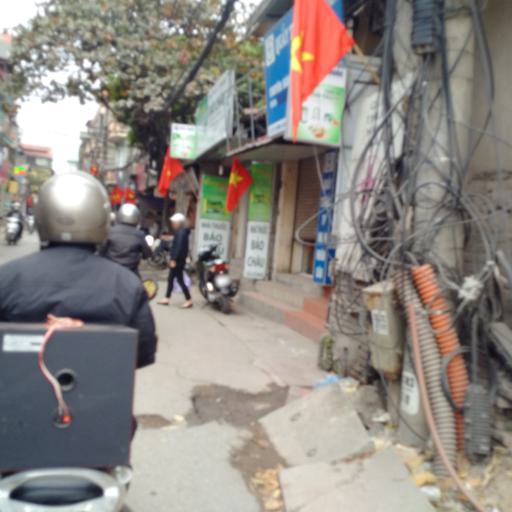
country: VN
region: Ha Noi
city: Cau Dien
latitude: 21.0561
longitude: 105.7822
